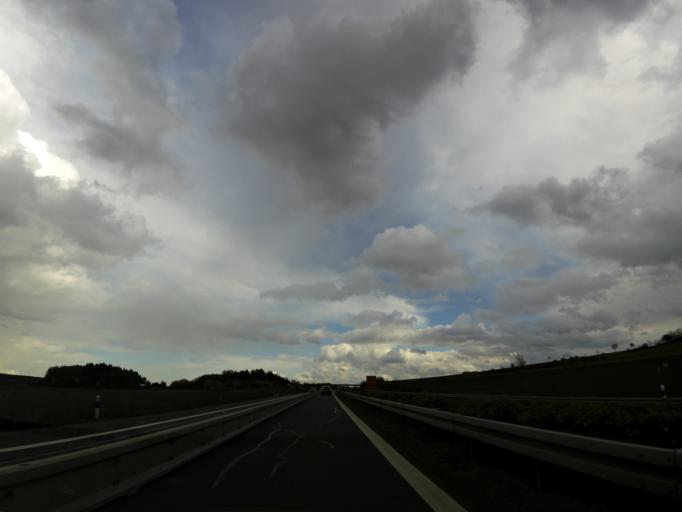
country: DE
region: Saxony-Anhalt
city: Derenburg
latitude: 51.8301
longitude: 10.9179
